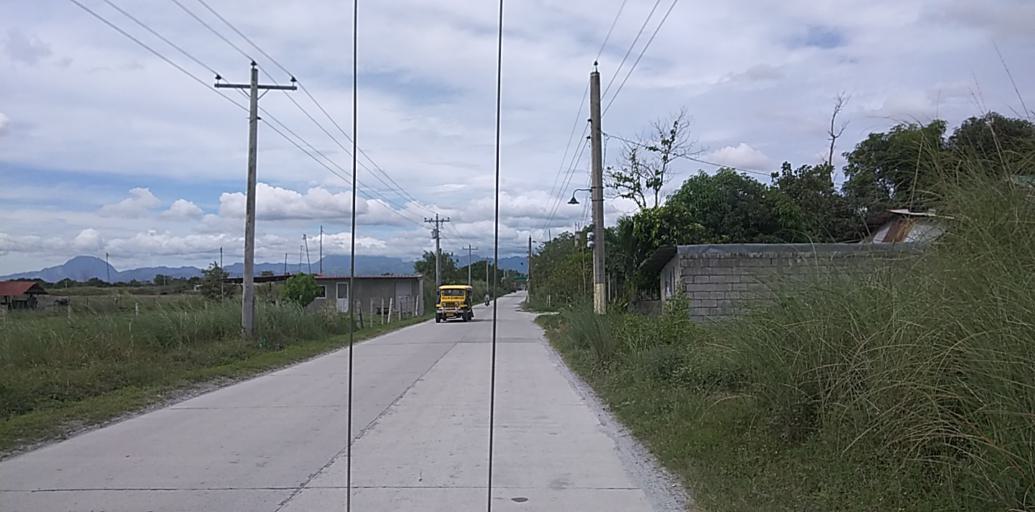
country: PH
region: Central Luzon
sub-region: Province of Pampanga
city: Balas
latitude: 15.0639
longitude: 120.5804
